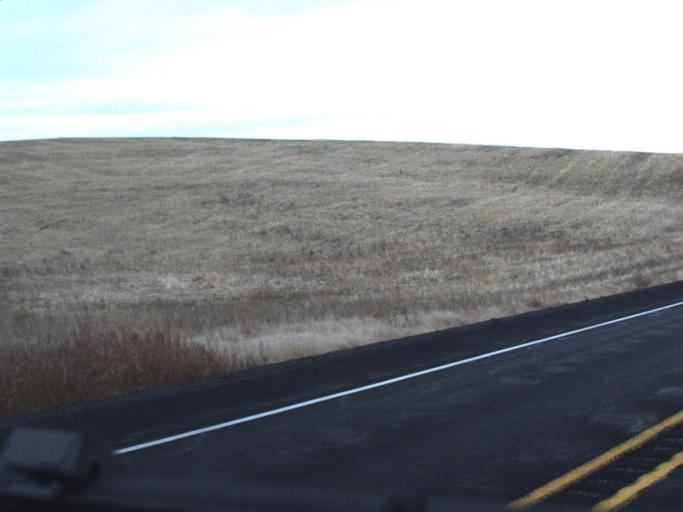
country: US
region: Washington
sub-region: Whitman County
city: Pullman
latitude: 46.6570
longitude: -117.1909
